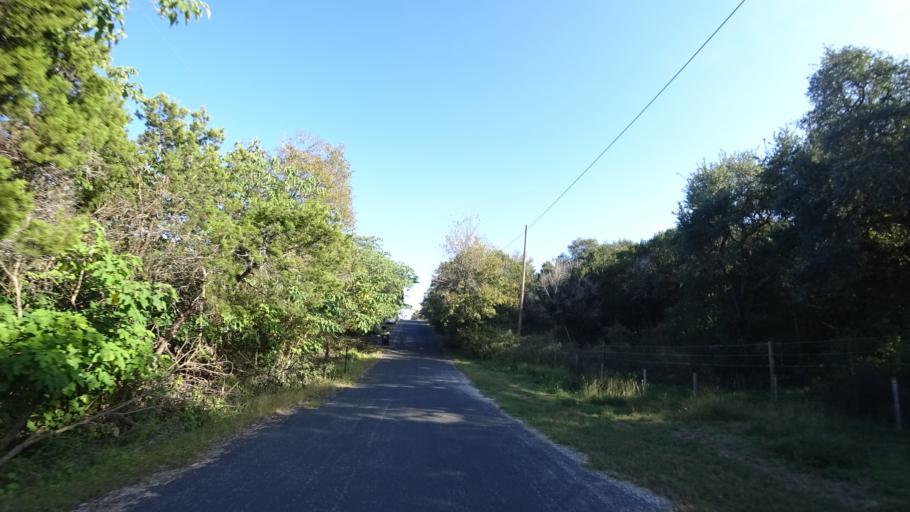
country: US
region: Texas
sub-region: Travis County
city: Barton Creek
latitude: 30.2401
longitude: -97.9120
